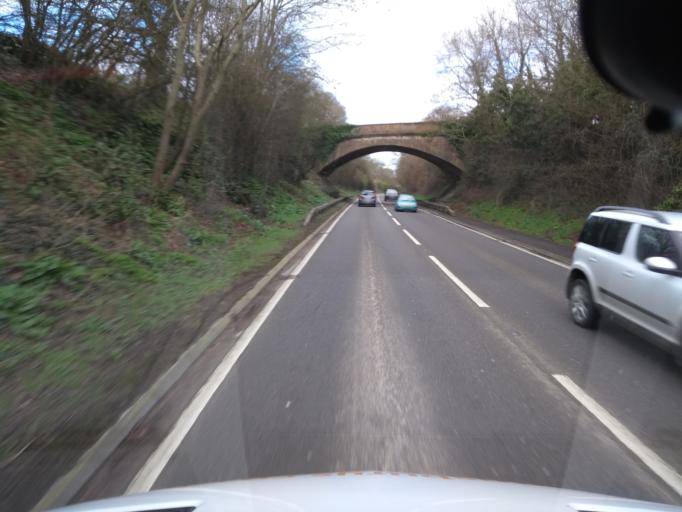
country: GB
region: England
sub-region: Somerset
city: Yeovil
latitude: 50.9425
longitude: -2.6824
